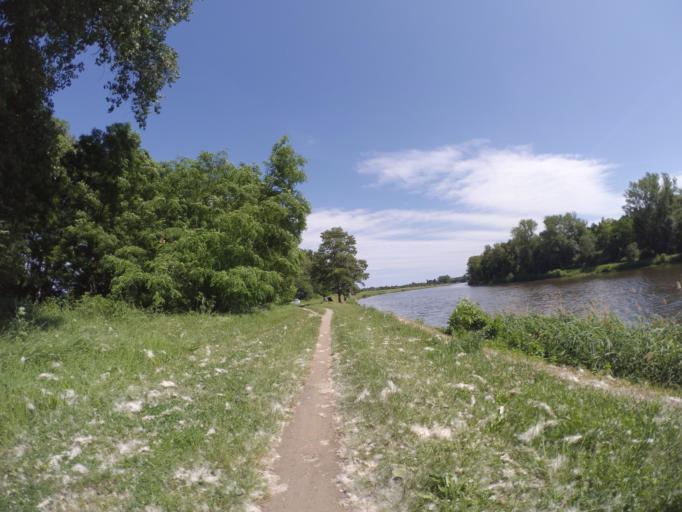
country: CZ
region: Central Bohemia
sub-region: Okres Nymburk
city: Sadska
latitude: 50.1682
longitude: 14.9500
